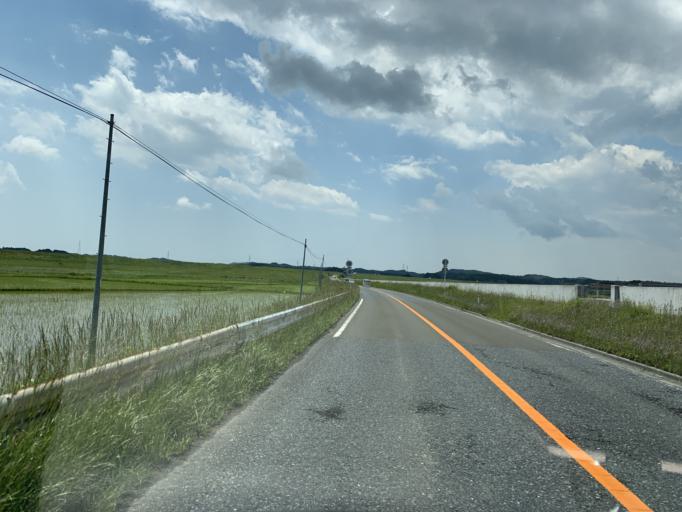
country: JP
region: Miyagi
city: Matsushima
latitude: 38.4464
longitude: 141.0805
